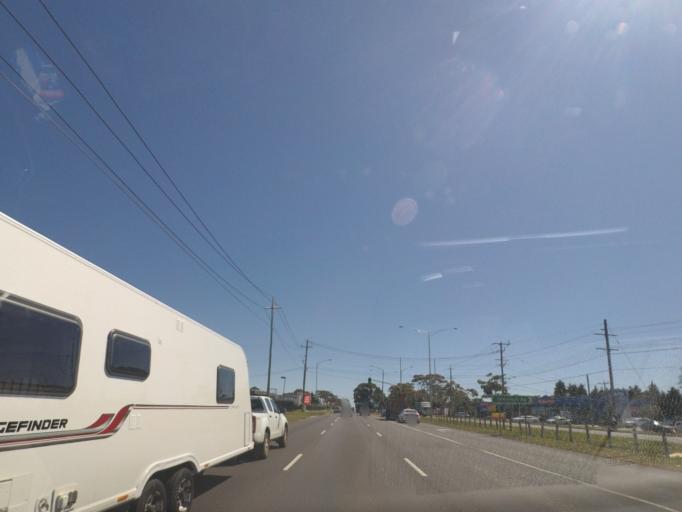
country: AU
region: Victoria
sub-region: Hume
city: Campbellfield
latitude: -37.6795
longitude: 144.9565
